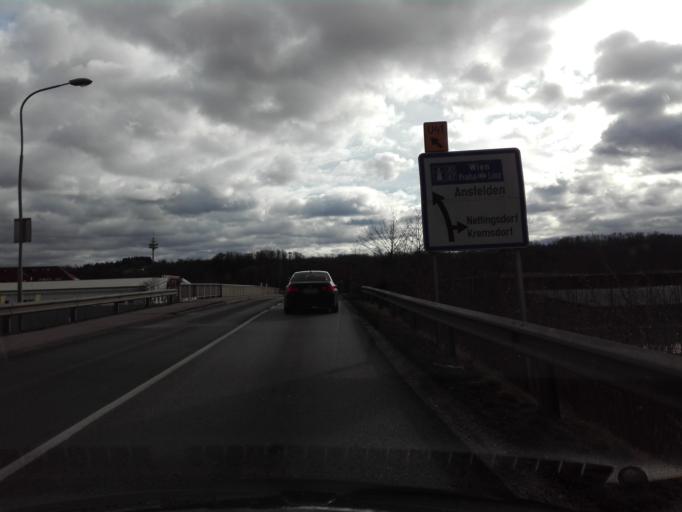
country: AT
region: Upper Austria
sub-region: Politischer Bezirk Linz-Land
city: Ansfelden
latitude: 48.2117
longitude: 14.2765
